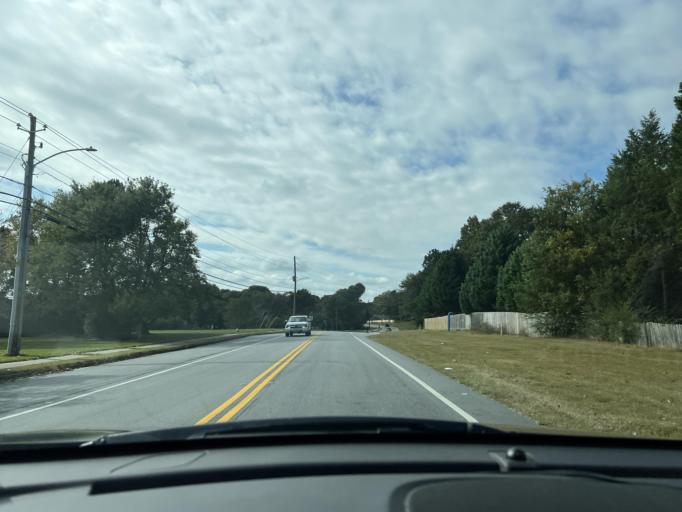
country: US
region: Georgia
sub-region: Gwinnett County
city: Grayson
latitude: 33.9014
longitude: -83.9483
